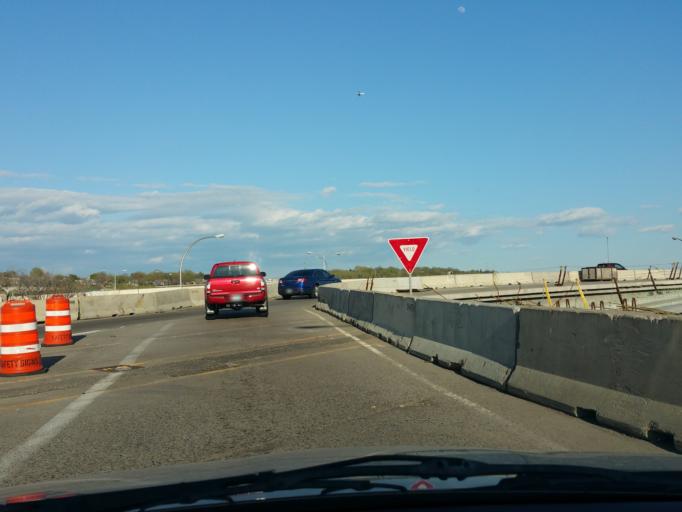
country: US
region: Minnesota
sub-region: Ramsey County
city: Saint Paul
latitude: 44.9531
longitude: -93.0832
